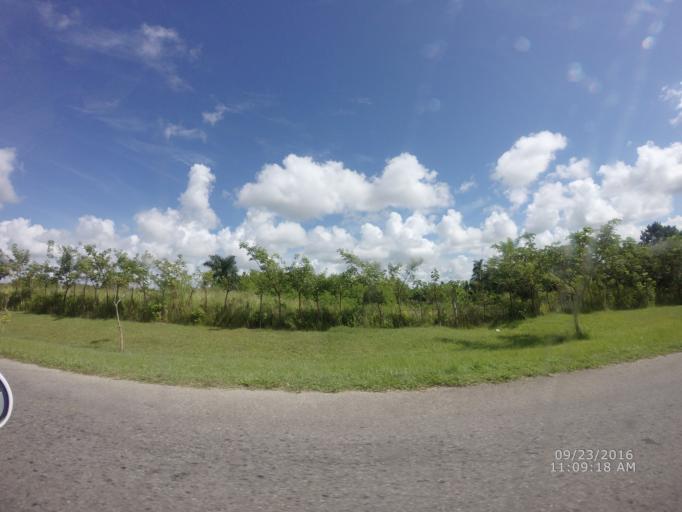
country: CU
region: La Habana
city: Arroyo Naranjo
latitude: 23.0176
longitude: -82.2429
